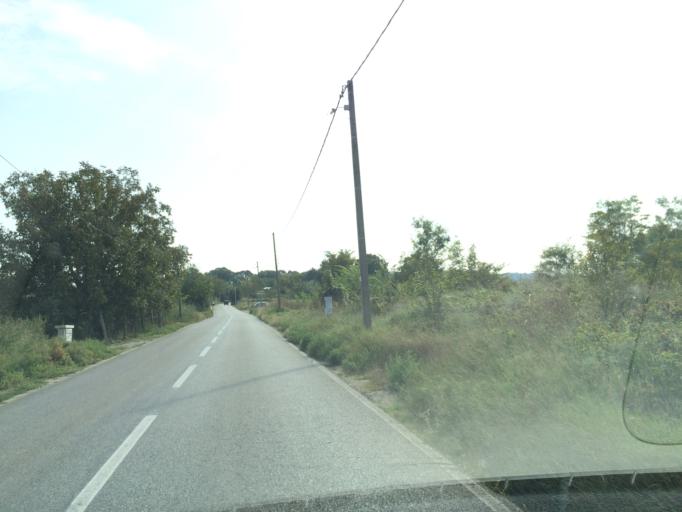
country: RS
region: Autonomna Pokrajina Vojvodina
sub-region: Juznobacki Okrug
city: Novi Sad
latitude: 45.2143
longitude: 19.8350
